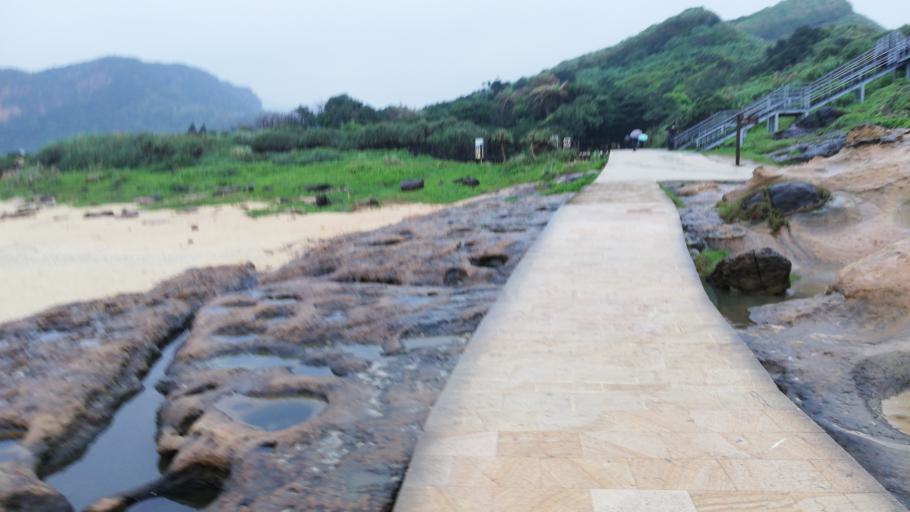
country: TW
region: Taiwan
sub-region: Keelung
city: Keelung
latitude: 25.2076
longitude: 121.6926
